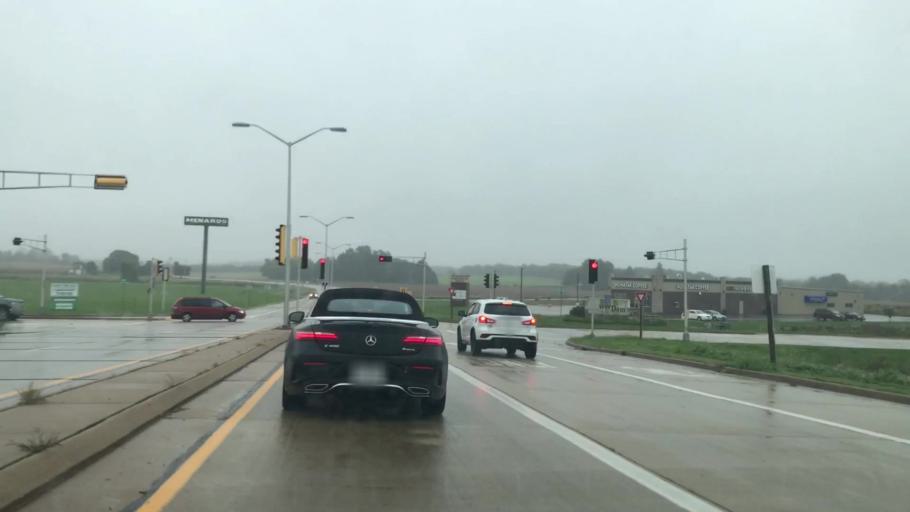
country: US
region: Wisconsin
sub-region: Dodge County
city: Beaver Dam
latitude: 43.4859
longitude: -88.8111
